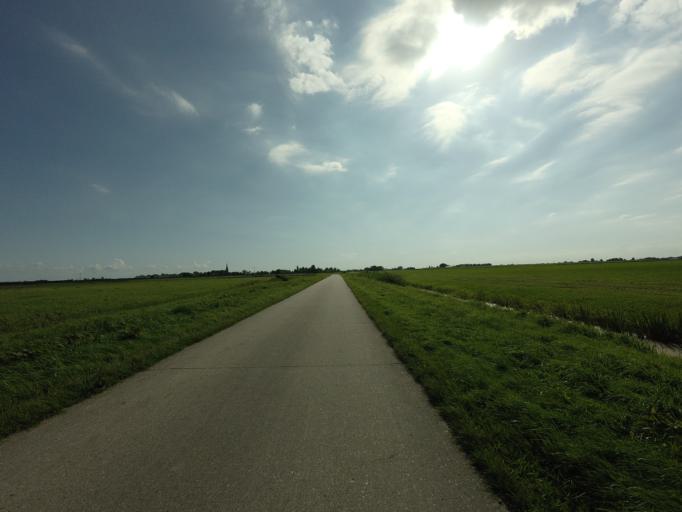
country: NL
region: Friesland
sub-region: Gemeente Littenseradiel
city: Makkum
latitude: 53.0841
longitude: 5.6322
